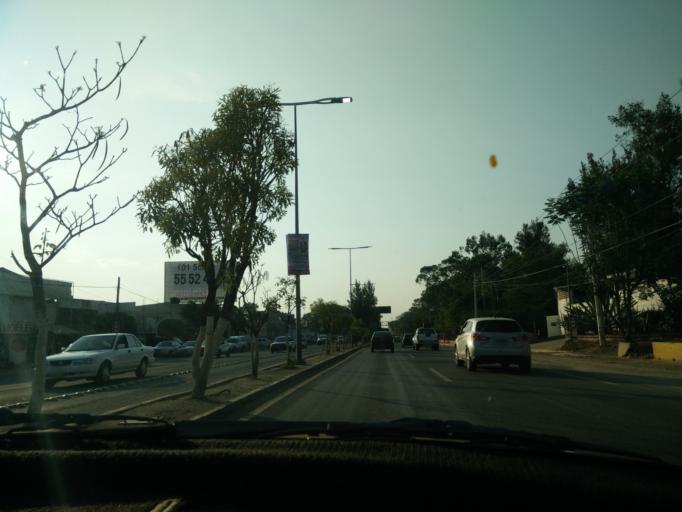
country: MX
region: Oaxaca
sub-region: Santa Maria Atzompa
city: San Jeronimo Yahuiche
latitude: 17.1163
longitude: -96.7592
